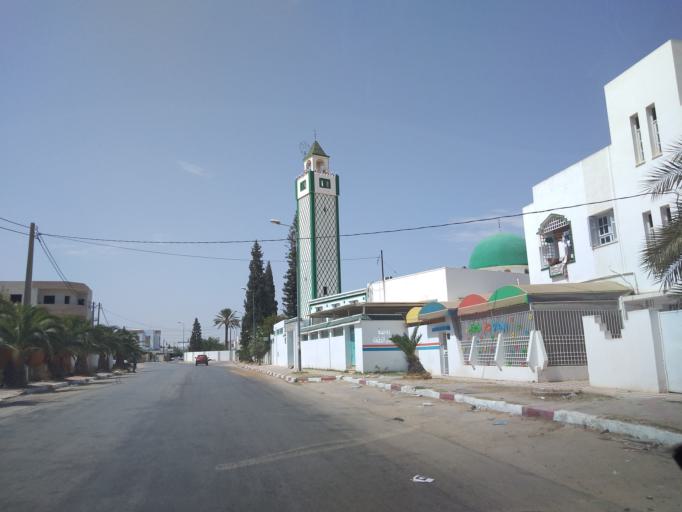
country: TN
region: Safaqis
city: Sfax
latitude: 34.7618
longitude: 10.7483
